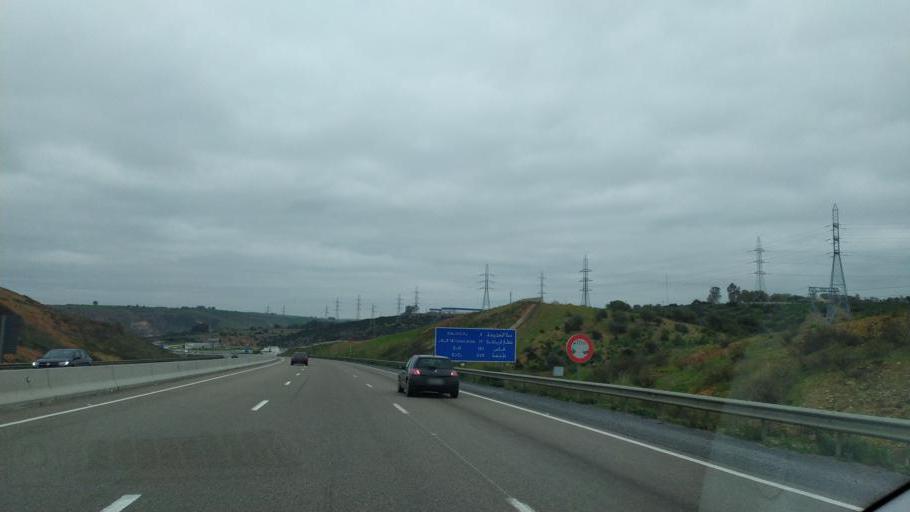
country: MA
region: Rabat-Sale-Zemmour-Zaer
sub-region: Rabat
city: Rabat
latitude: 33.9247
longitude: -6.7655
